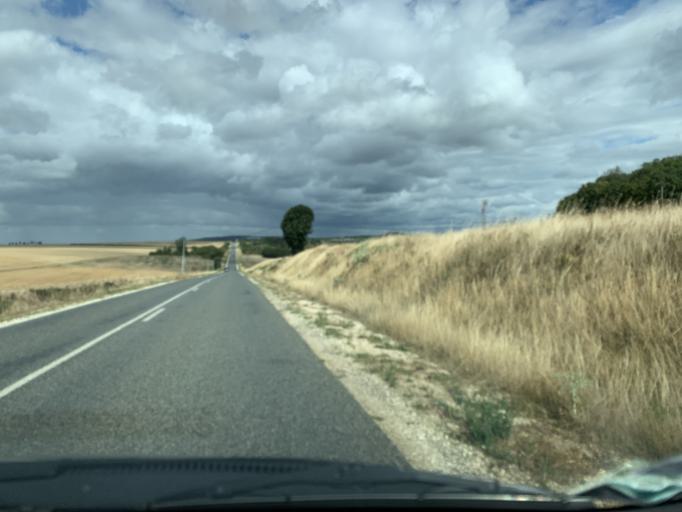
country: FR
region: Bourgogne
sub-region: Departement de la Nievre
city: Clamecy
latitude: 47.4298
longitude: 3.4782
